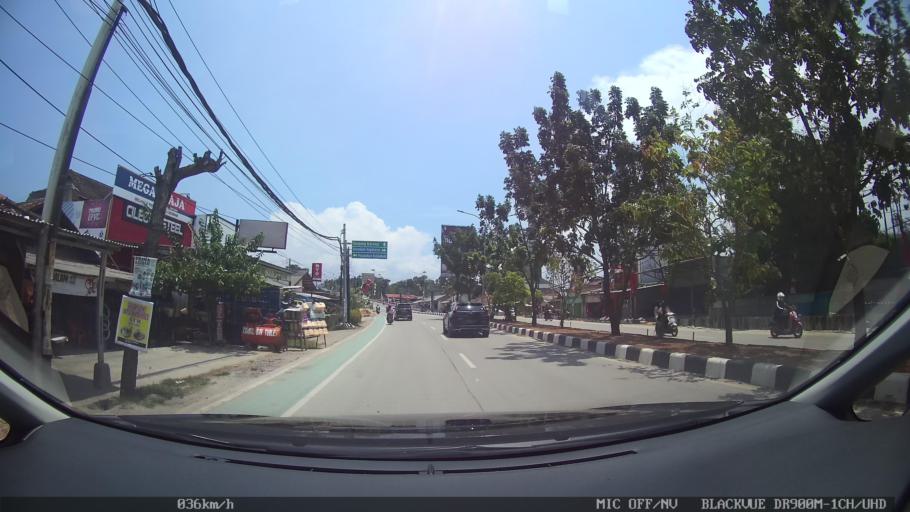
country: ID
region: Lampung
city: Kedaton
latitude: -5.3804
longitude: 105.2879
